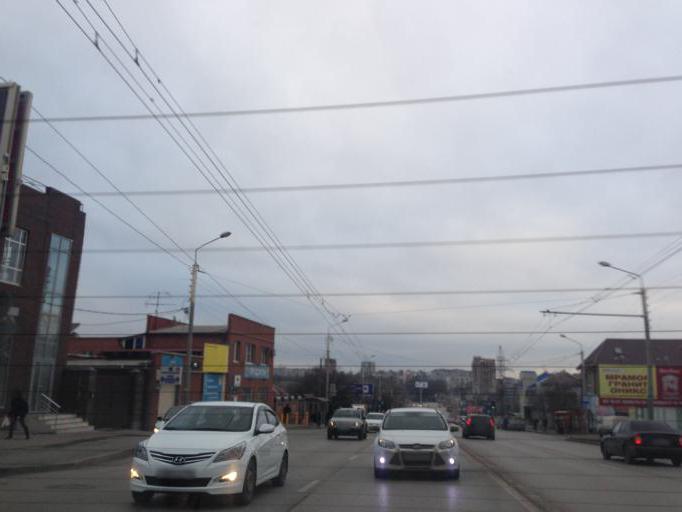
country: RU
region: Rostov
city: Severnyy
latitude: 47.2962
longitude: 39.7273
